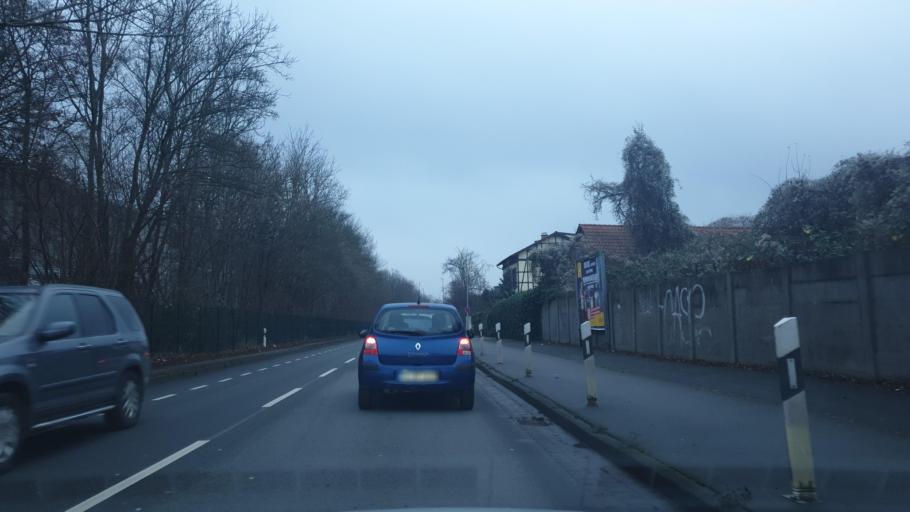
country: DE
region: North Rhine-Westphalia
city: Porta Westfalica
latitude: 52.2534
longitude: 8.9287
